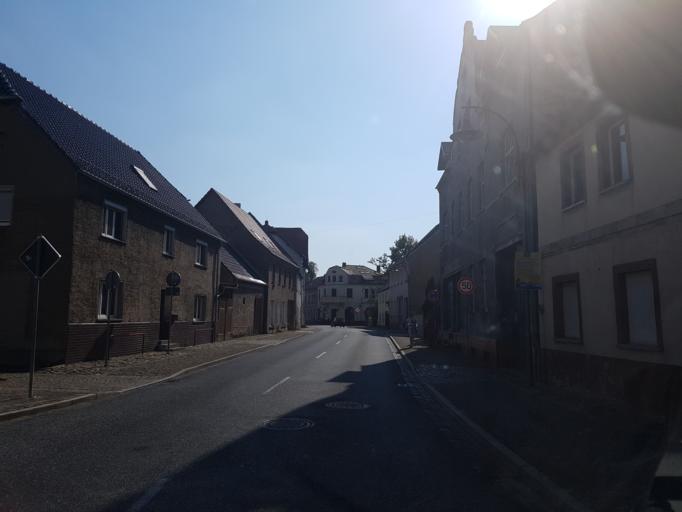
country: DE
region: Saxony-Anhalt
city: Annaburg
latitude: 51.7322
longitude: 13.0446
